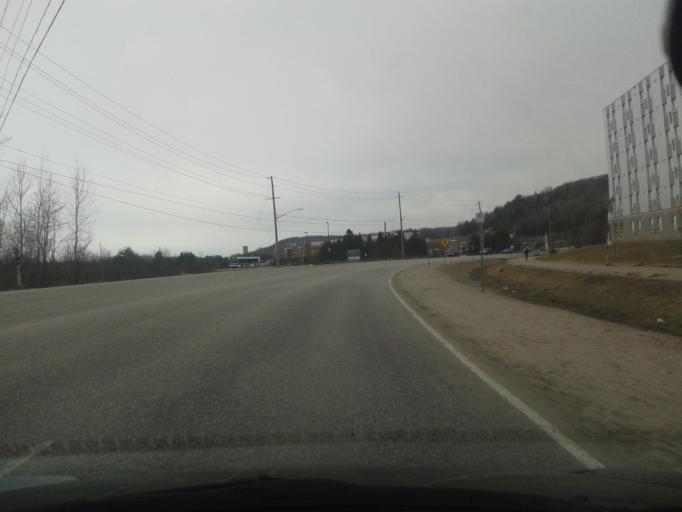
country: CA
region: Ontario
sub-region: Nipissing District
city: North Bay
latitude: 46.3342
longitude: -79.4908
